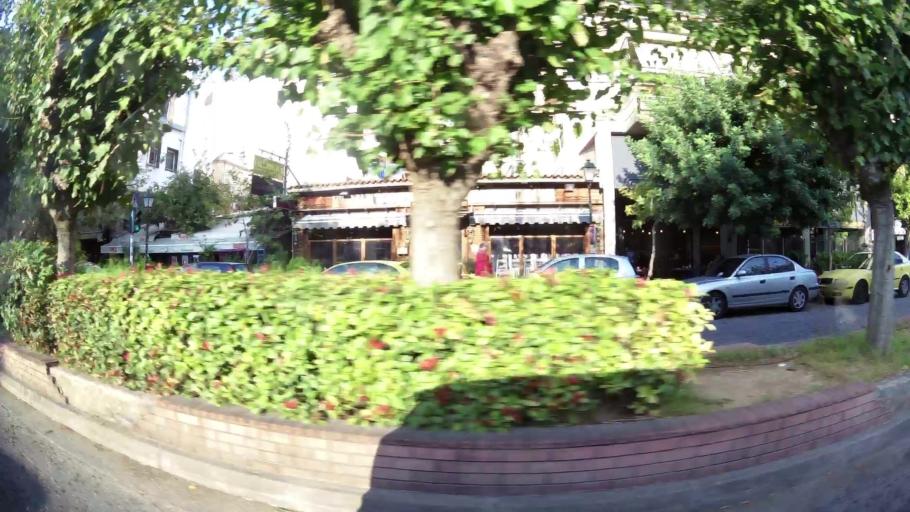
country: GR
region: Attica
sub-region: Nomarchia Athinas
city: Kaisariani
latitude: 37.9780
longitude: 23.7624
